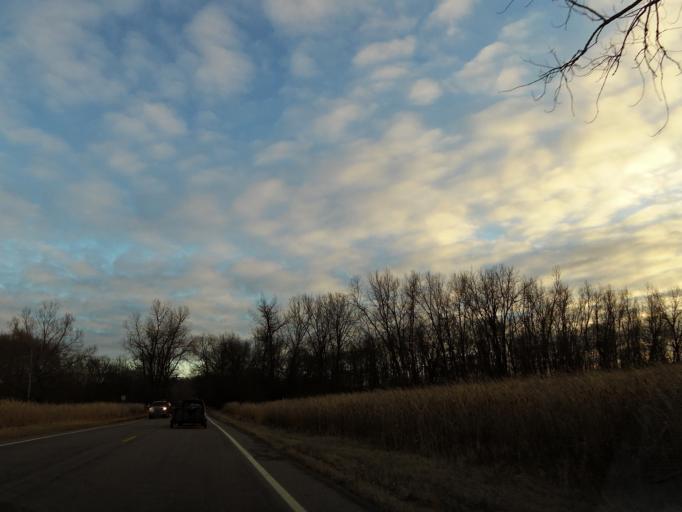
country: US
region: Minnesota
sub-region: Washington County
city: Dellwood
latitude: 45.0839
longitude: -92.9675
